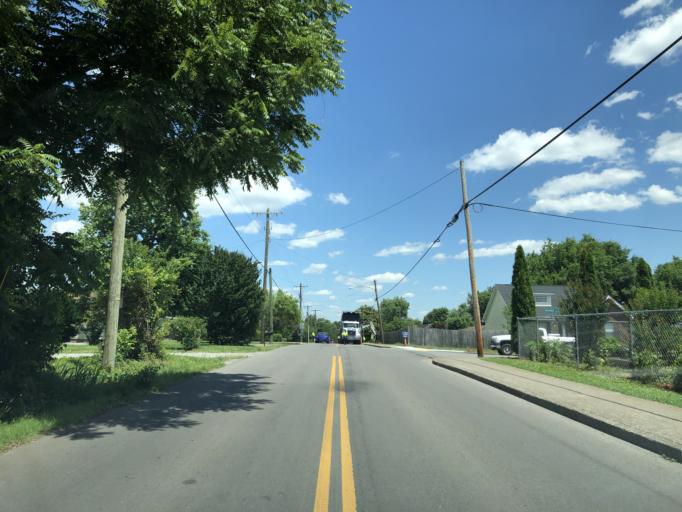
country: US
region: Tennessee
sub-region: Davidson County
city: Nashville
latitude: 36.1866
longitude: -86.7202
